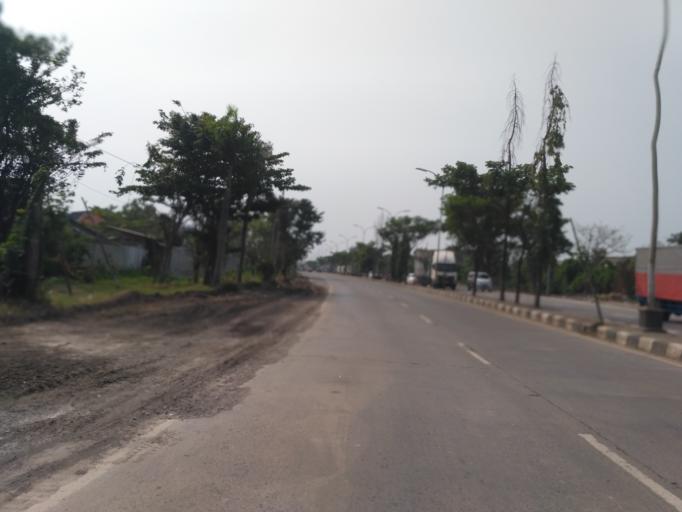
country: ID
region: Central Java
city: Semarang
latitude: -6.9667
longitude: 110.3935
